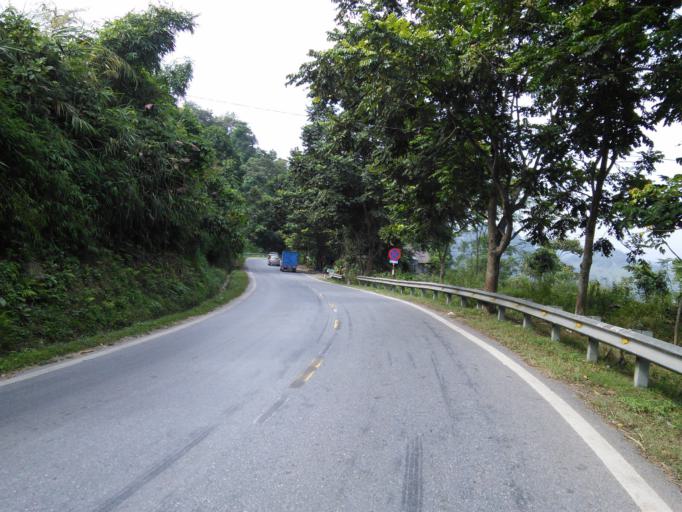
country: VN
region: Lao Cai
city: Lao Cai
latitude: 22.4450
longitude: 103.9381
